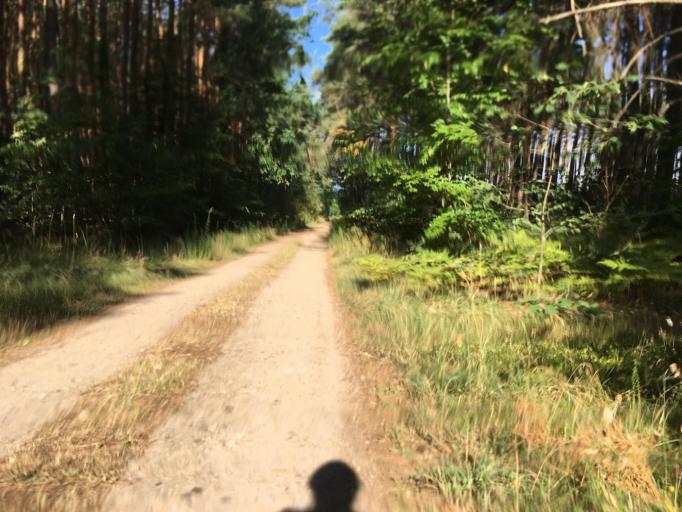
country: DE
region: Brandenburg
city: Liebenwalde
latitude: 52.9081
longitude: 13.4720
